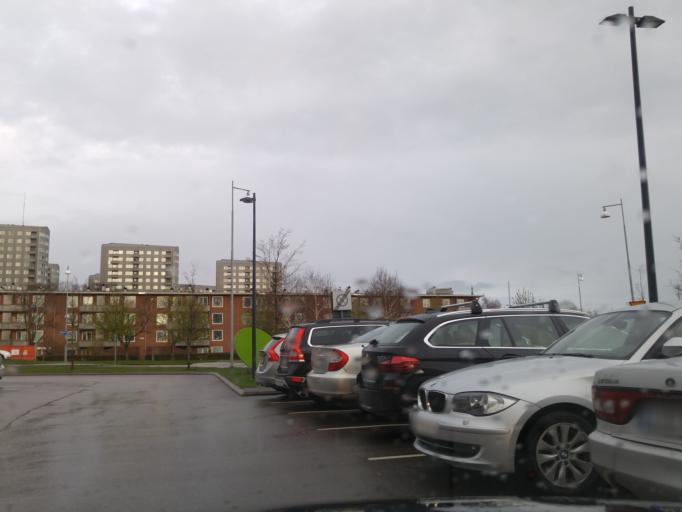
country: SE
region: Vaestra Goetaland
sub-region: Goteborg
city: Majorna
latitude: 57.6507
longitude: 11.9141
